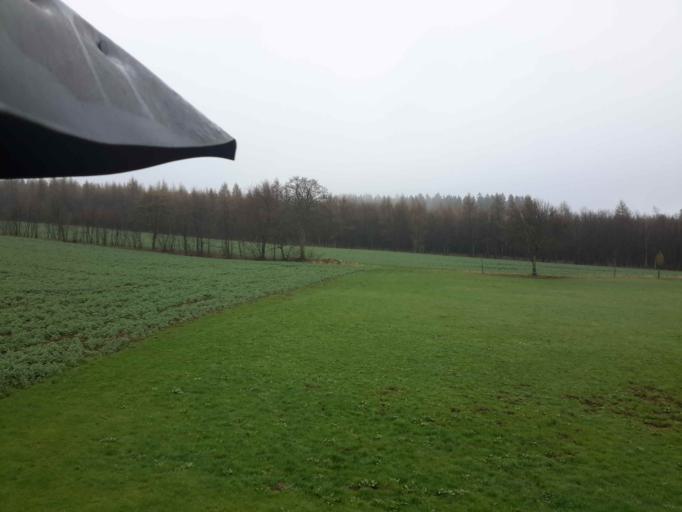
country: DE
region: Saxony
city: Sayda
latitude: 50.7199
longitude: 13.4173
